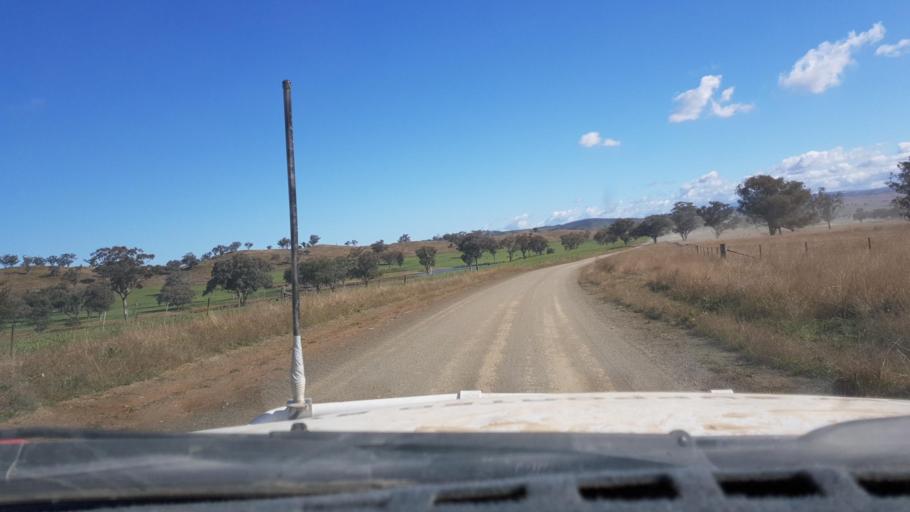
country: AU
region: New South Wales
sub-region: Narrabri
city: Blair Athol
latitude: -30.5477
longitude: 150.4575
